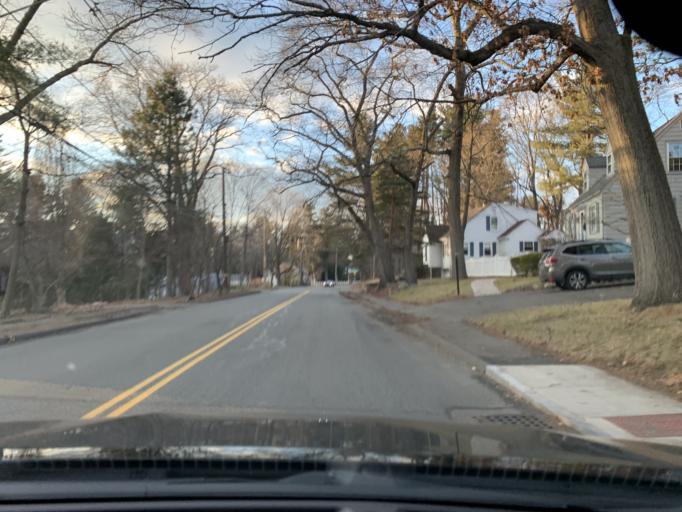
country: US
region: Massachusetts
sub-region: Essex County
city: Lynnfield
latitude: 42.5294
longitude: -71.0370
